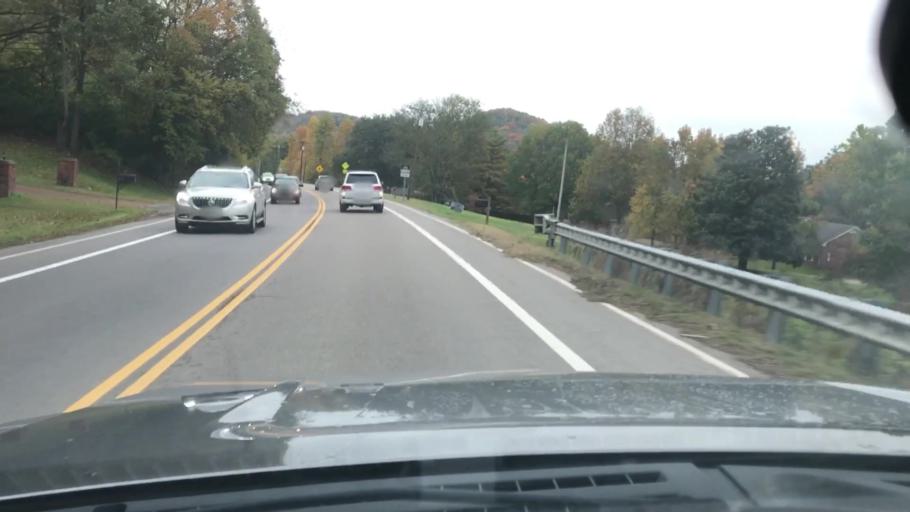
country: US
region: Tennessee
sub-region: Davidson County
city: Forest Hills
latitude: 36.0179
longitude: -86.8881
